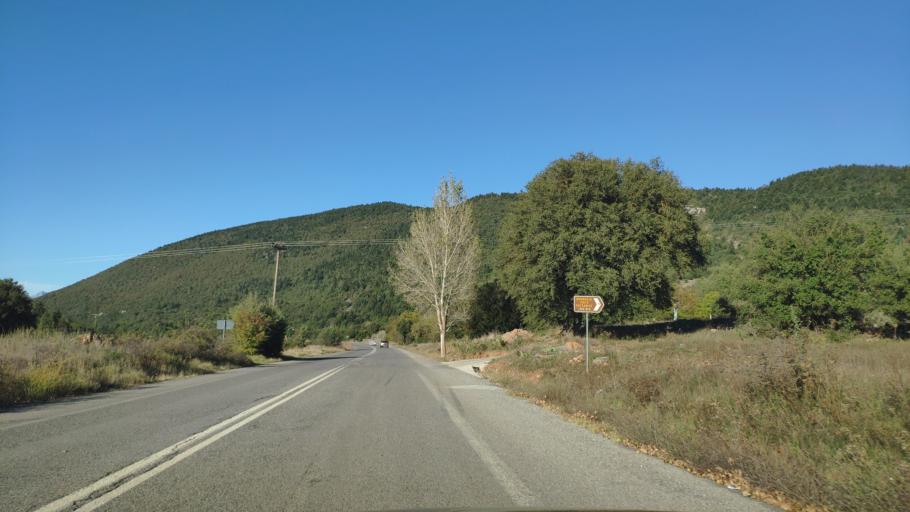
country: GR
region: Peloponnese
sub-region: Nomos Arkadias
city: Langadhia
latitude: 37.6934
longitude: 22.1972
